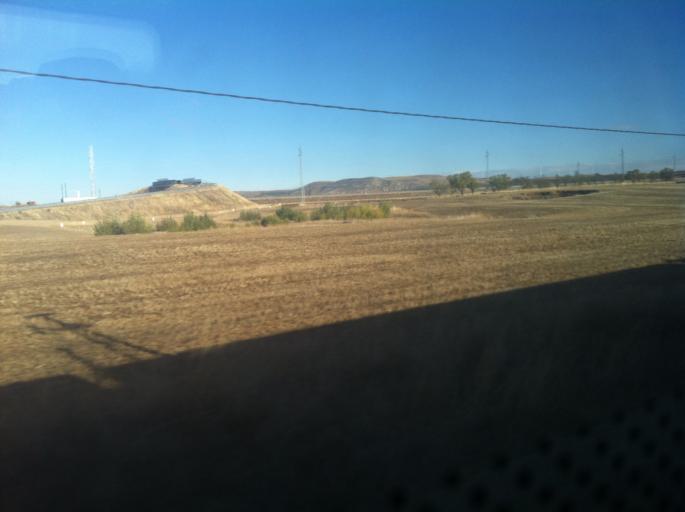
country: ES
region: Castille and Leon
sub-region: Provincia de Burgos
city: Villamedianilla
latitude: 42.1337
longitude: -4.1297
